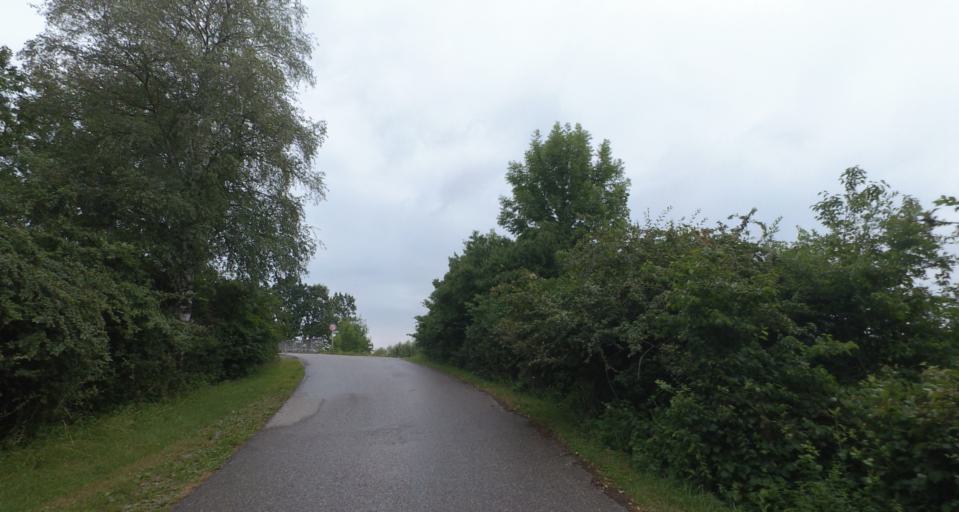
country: DE
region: Bavaria
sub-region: Upper Bavaria
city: Grabenstatt
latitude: 47.8224
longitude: 12.5268
